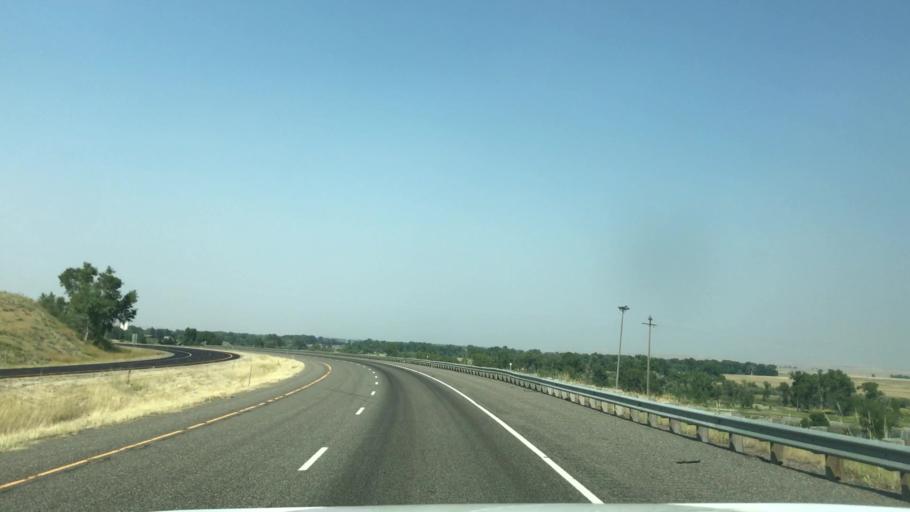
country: US
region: Montana
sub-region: Cascade County
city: Sun Prairie
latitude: 47.2487
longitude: -111.7126
